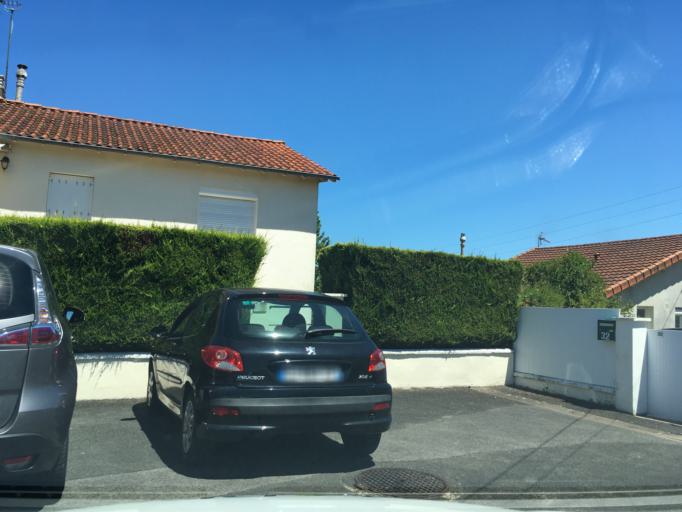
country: FR
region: Poitou-Charentes
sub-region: Departement des Deux-Sevres
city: Niort
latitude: 46.3334
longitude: -0.4355
